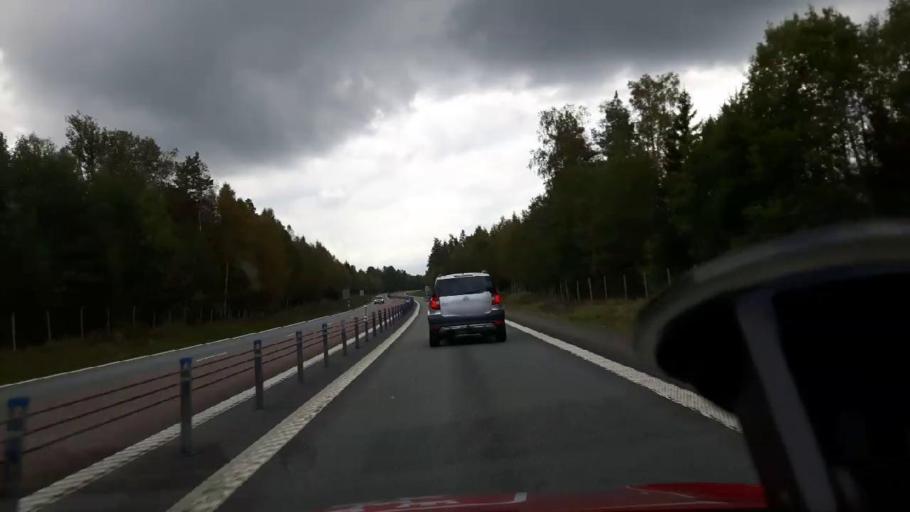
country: SE
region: Gaevleborg
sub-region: Gavle Kommun
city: Gavle
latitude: 60.7690
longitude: 17.0736
